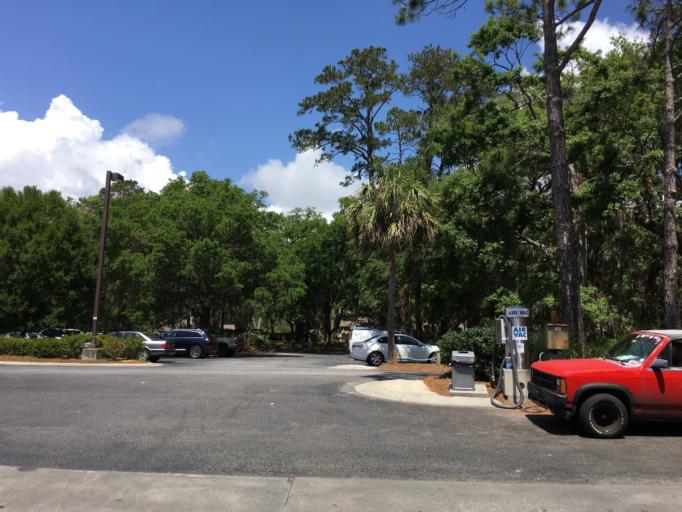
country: US
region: South Carolina
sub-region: Beaufort County
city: Hilton Head Island
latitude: 32.1310
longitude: -80.8001
